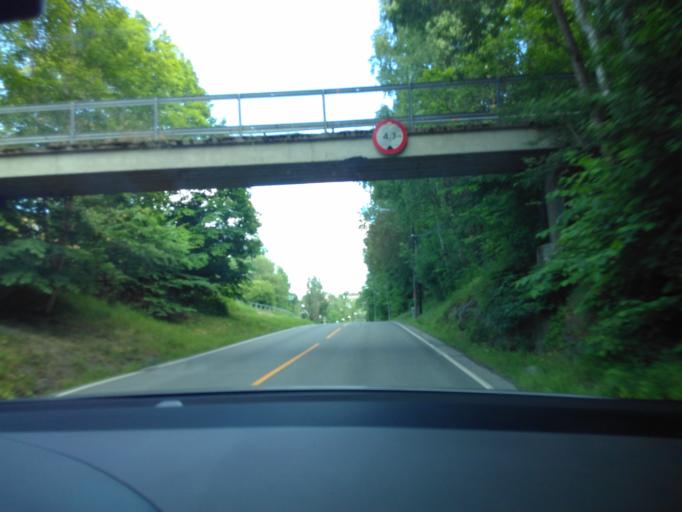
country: NO
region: Akershus
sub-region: Baerum
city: Lysaker
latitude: 59.9388
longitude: 10.6046
